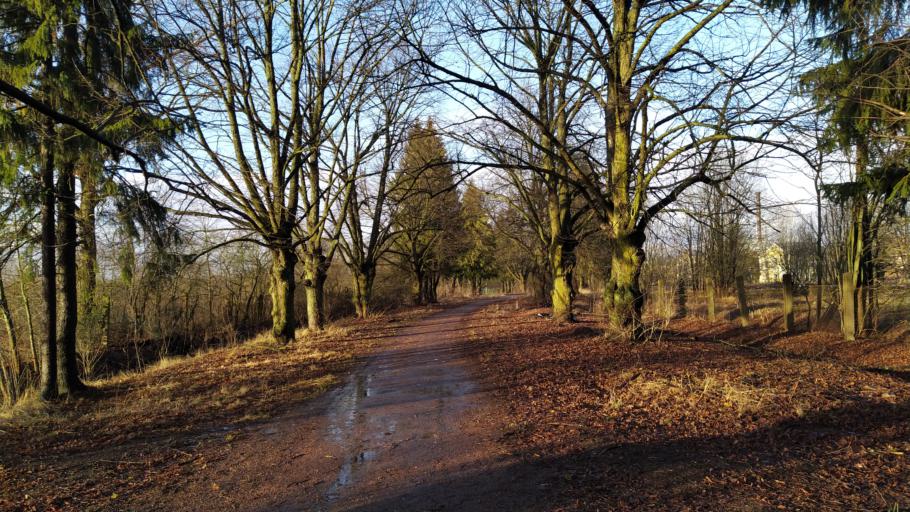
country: RU
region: St.-Petersburg
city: Pushkin
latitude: 59.7266
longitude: 30.3877
